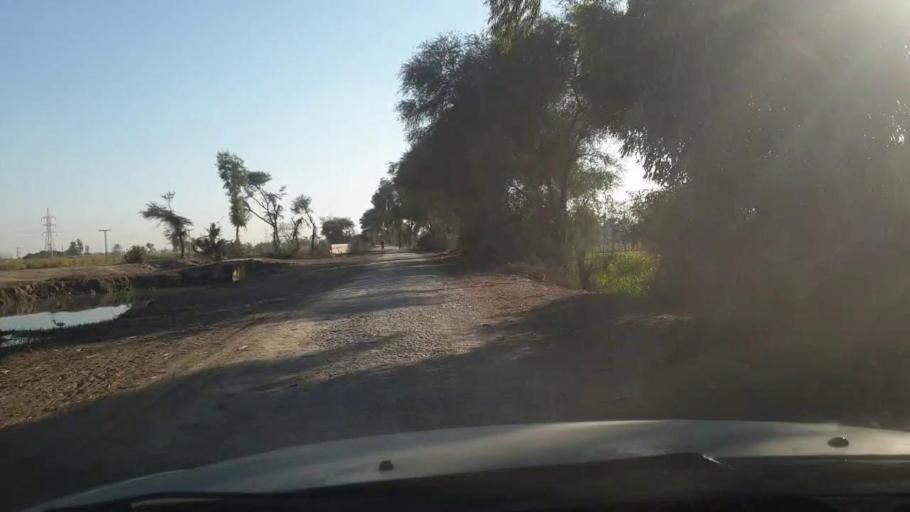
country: PK
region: Sindh
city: Ghotki
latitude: 28.0344
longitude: 69.3234
